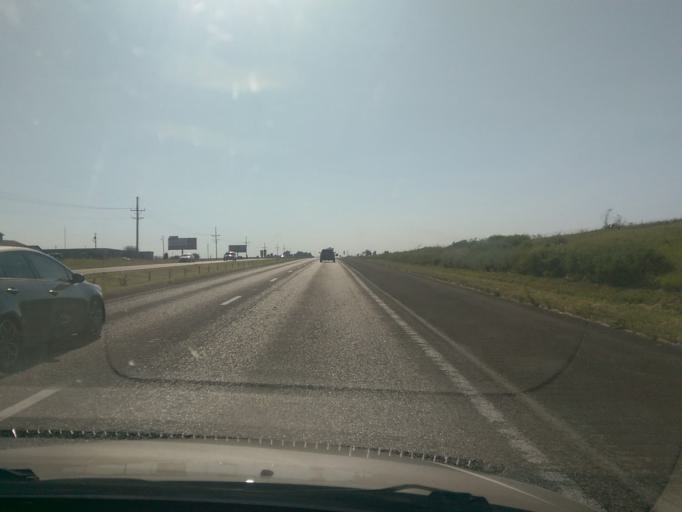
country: US
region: Missouri
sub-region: Lafayette County
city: Concordia
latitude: 38.9884
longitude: -93.5316
